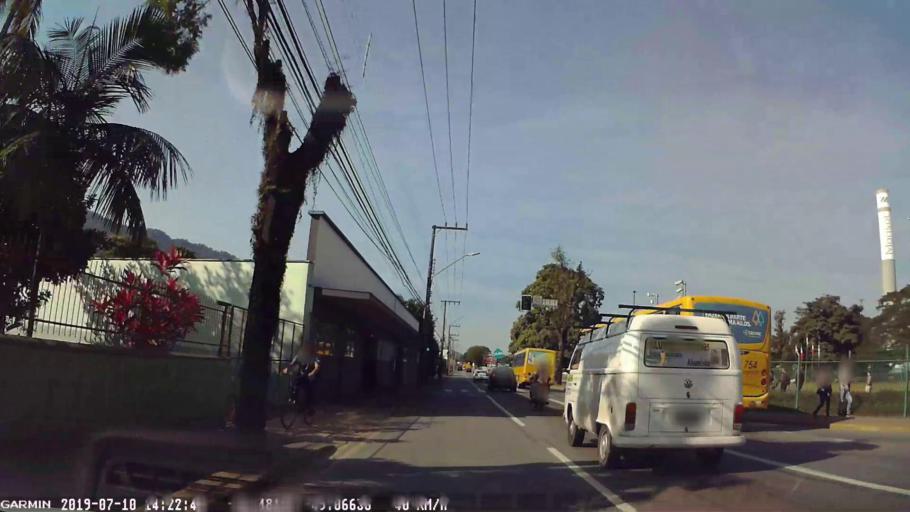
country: BR
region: Santa Catarina
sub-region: Jaragua Do Sul
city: Jaragua do Sul
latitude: -26.4817
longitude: -49.0664
